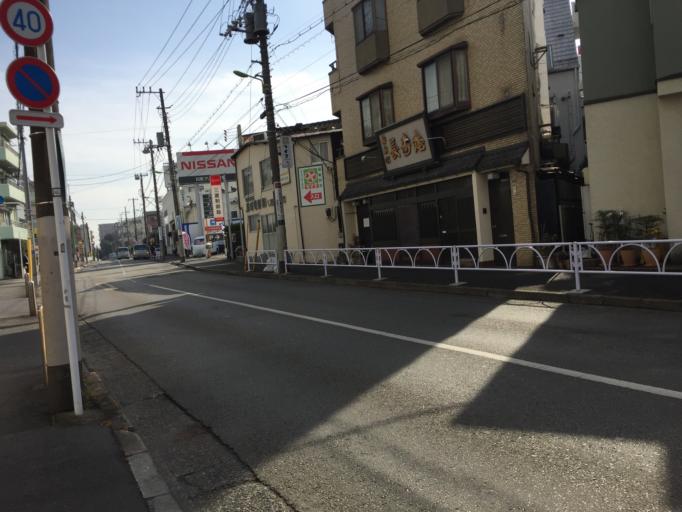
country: JP
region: Tokyo
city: Tokyo
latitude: 35.6329
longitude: 139.6384
